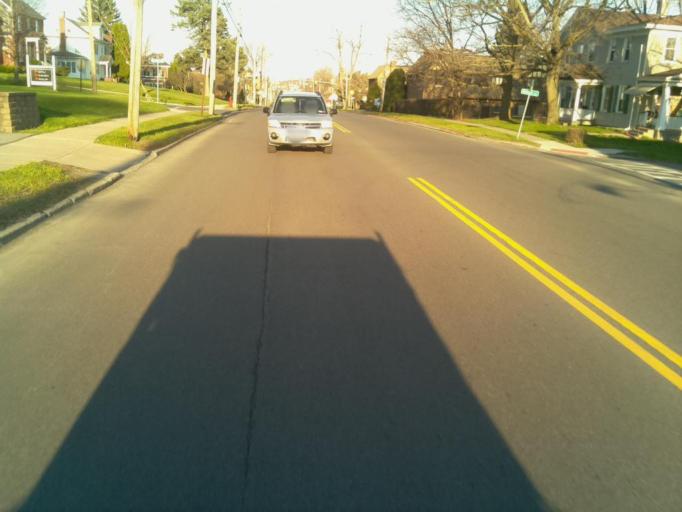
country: US
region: New York
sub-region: Onondaga County
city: East Syracuse
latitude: 43.0692
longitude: -76.0983
